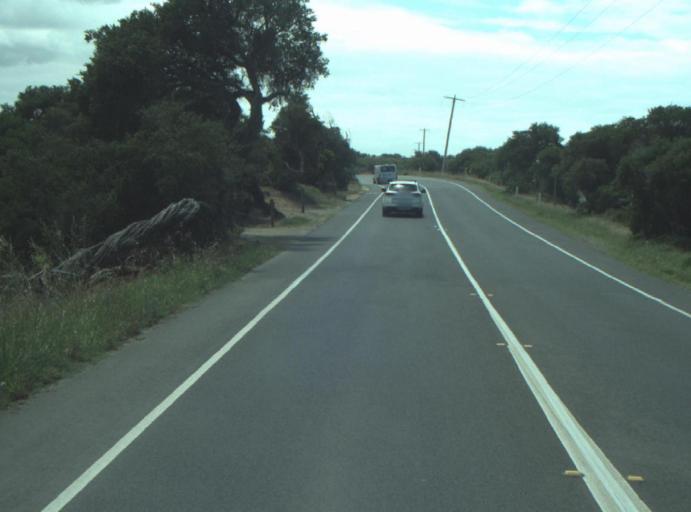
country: AU
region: Victoria
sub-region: Greater Geelong
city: Leopold
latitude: -38.2807
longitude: 144.5001
